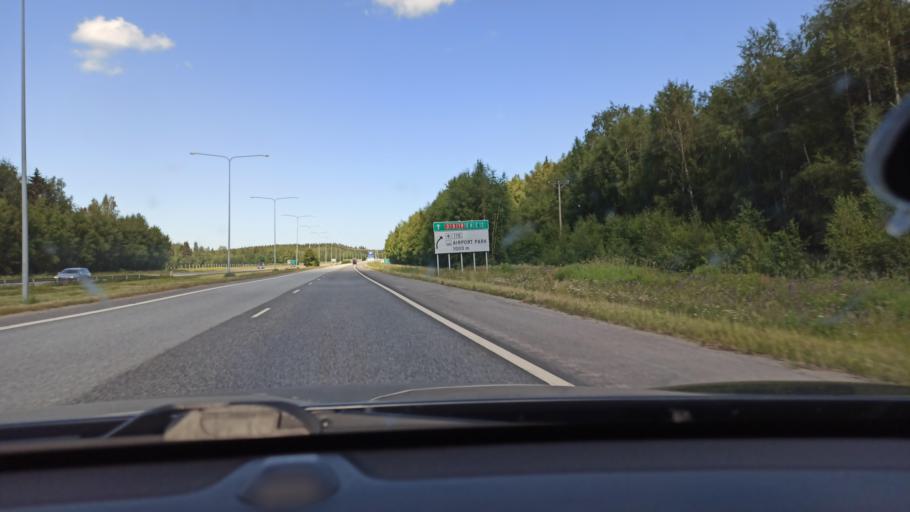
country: FI
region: Ostrobothnia
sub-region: Vaasa
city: Ristinummi
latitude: 63.0422
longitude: 21.7289
